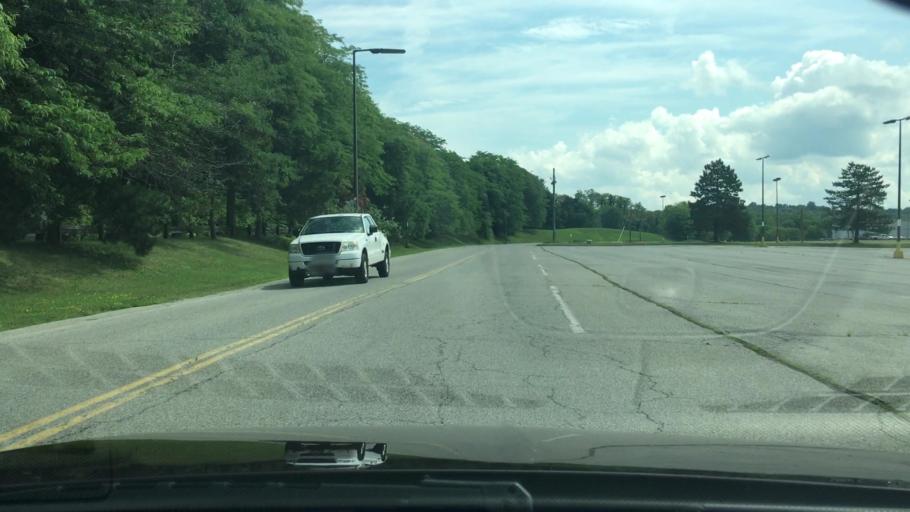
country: US
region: New York
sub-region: Dutchess County
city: Brinckerhoff
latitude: 41.5449
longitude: -73.8275
